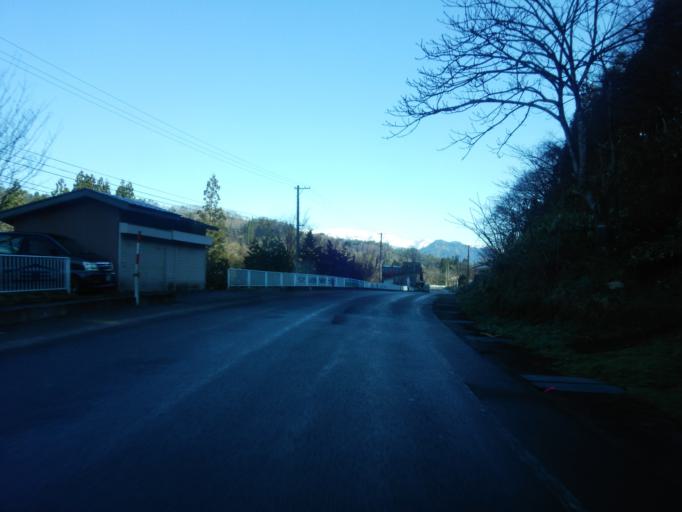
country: JP
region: Fukushima
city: Kitakata
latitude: 37.6838
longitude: 139.7892
